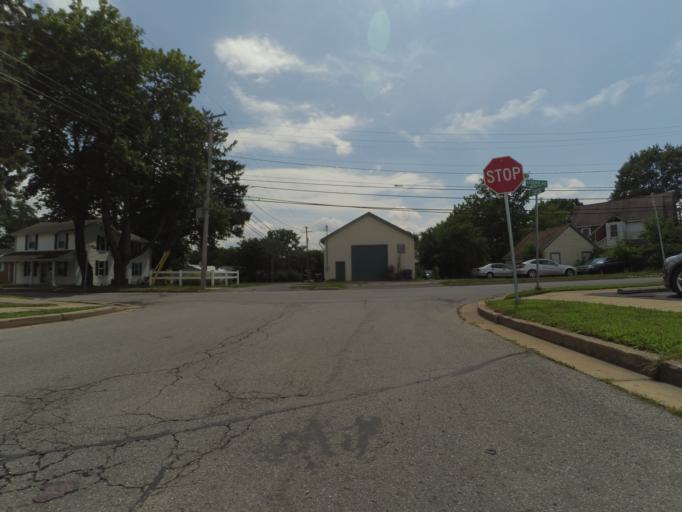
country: US
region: Pennsylvania
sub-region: Centre County
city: State College
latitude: 40.7865
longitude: -77.8542
